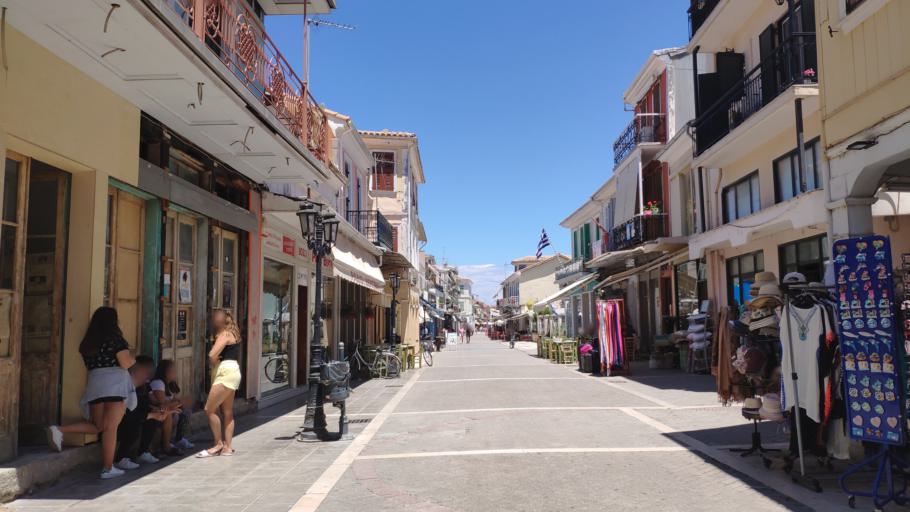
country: GR
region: Ionian Islands
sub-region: Lefkada
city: Lefkada
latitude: 38.8314
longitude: 20.7052
